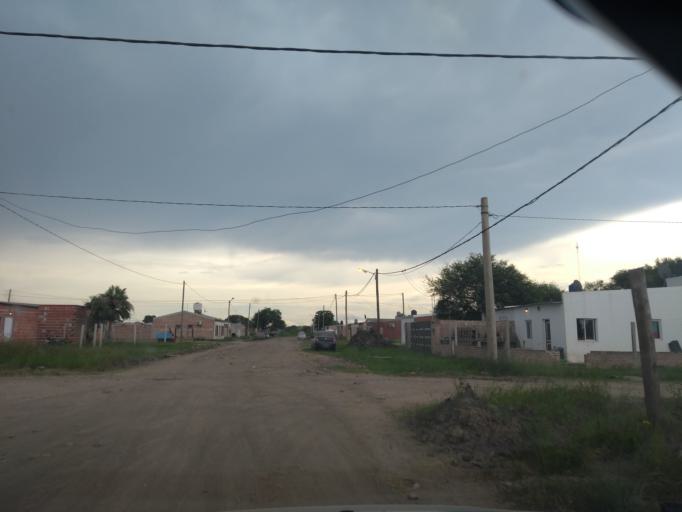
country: AR
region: Chaco
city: Resistencia
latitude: -27.4666
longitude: -59.0305
